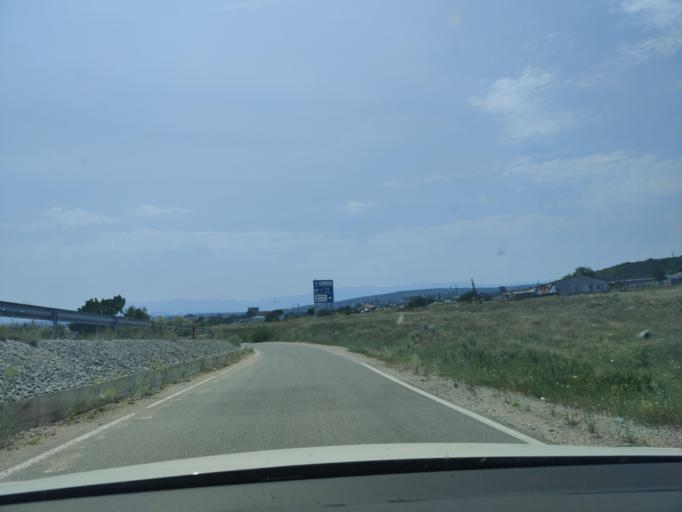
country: BG
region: Montana
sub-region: Obshtina Montana
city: Montana
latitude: 43.4360
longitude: 23.2320
